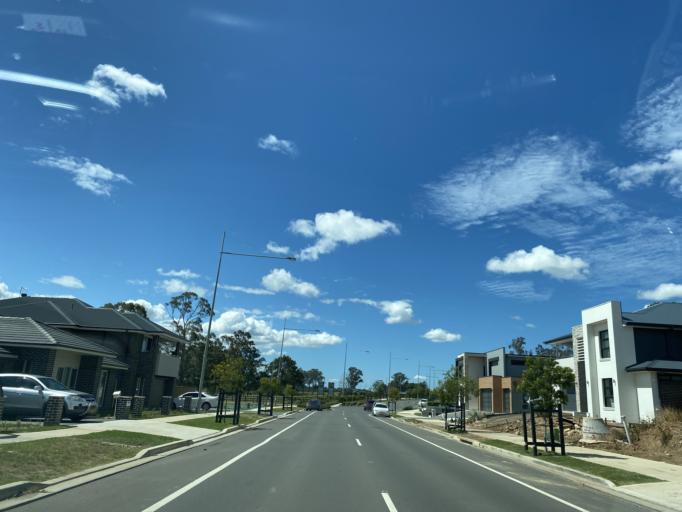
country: AU
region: New South Wales
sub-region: Campbelltown Municipality
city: Leumeah
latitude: -34.0130
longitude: 150.7894
